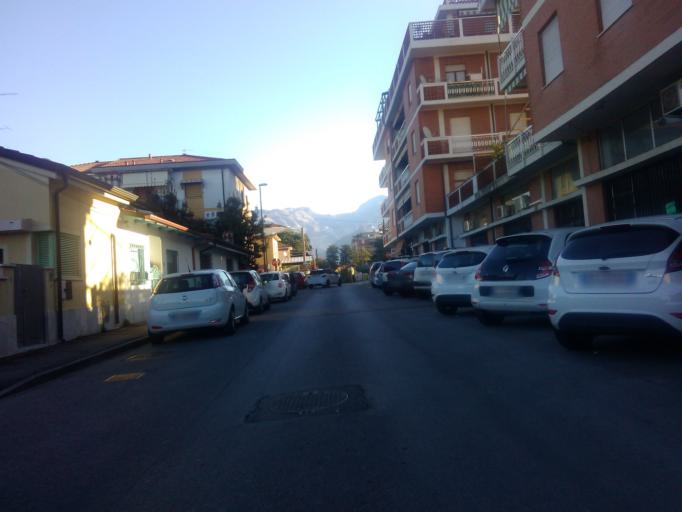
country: IT
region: Tuscany
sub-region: Provincia di Massa-Carrara
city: Carrara
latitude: 44.0505
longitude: 10.0568
